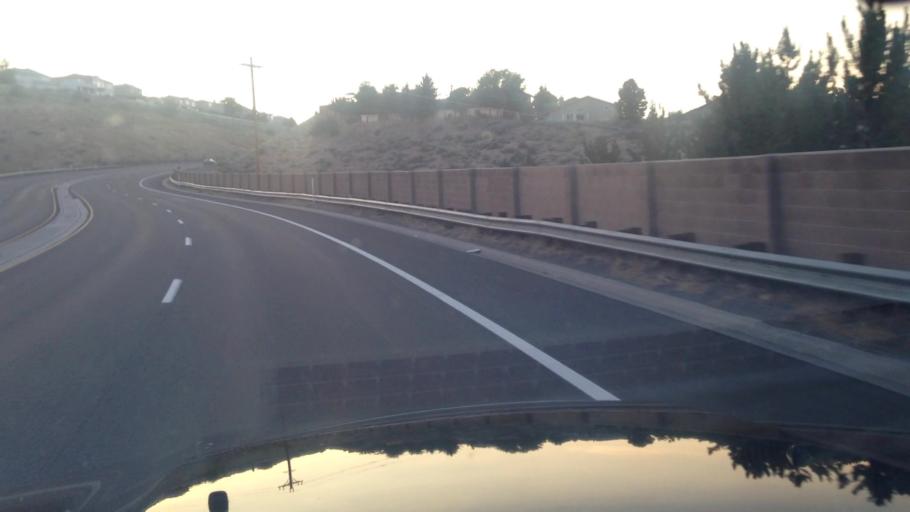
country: US
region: Nevada
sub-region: Washoe County
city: Reno
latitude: 39.4802
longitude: -119.8470
